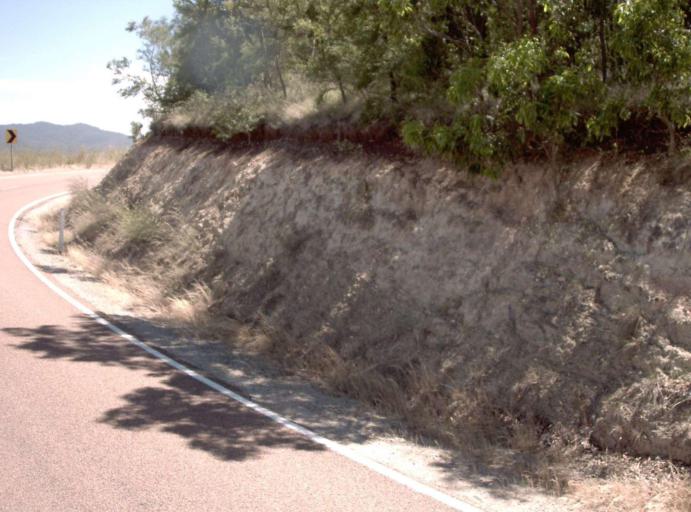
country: AU
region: Victoria
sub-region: East Gippsland
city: Lakes Entrance
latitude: -37.4780
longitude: 148.1810
